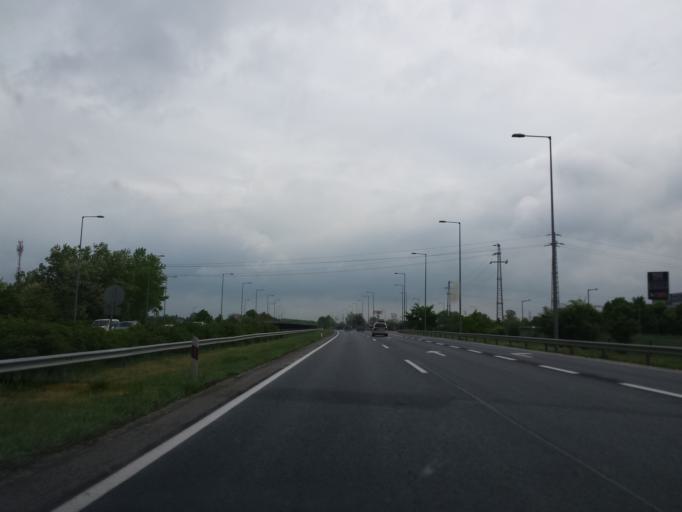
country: HU
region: Pest
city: Toeroekbalint
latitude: 47.4549
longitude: 18.9031
